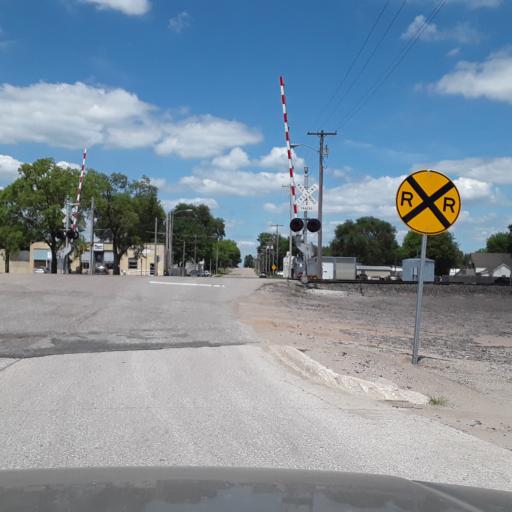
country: US
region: Nebraska
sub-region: Platte County
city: Columbus
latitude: 41.3885
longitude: -97.4932
